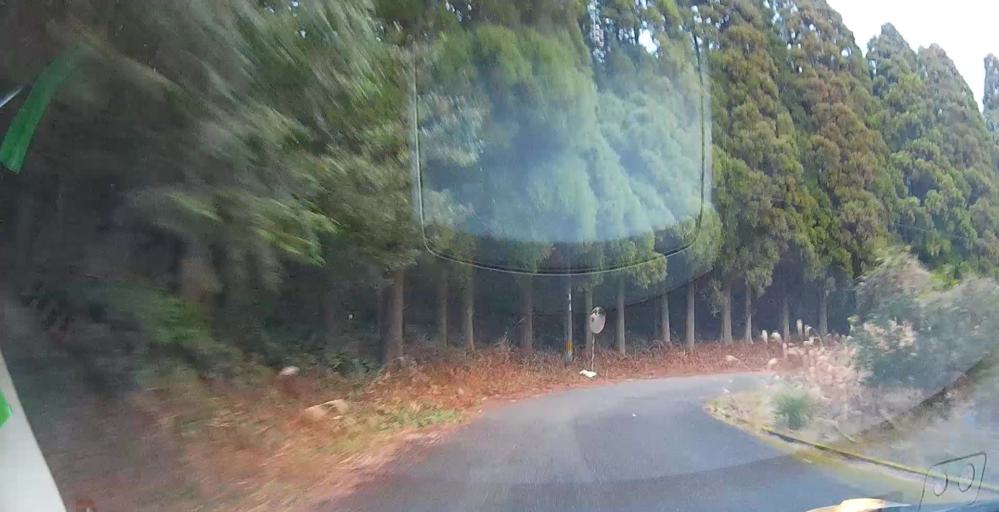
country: JP
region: Kagoshima
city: Izumi
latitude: 32.1199
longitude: 130.4157
